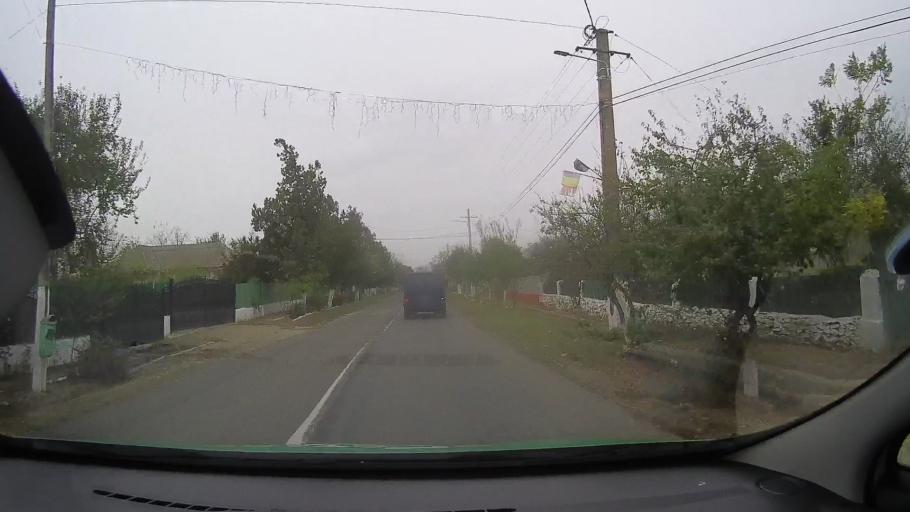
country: RO
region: Constanta
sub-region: Comuna Vulturu
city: Vulturu
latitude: 44.7027
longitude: 28.2345
